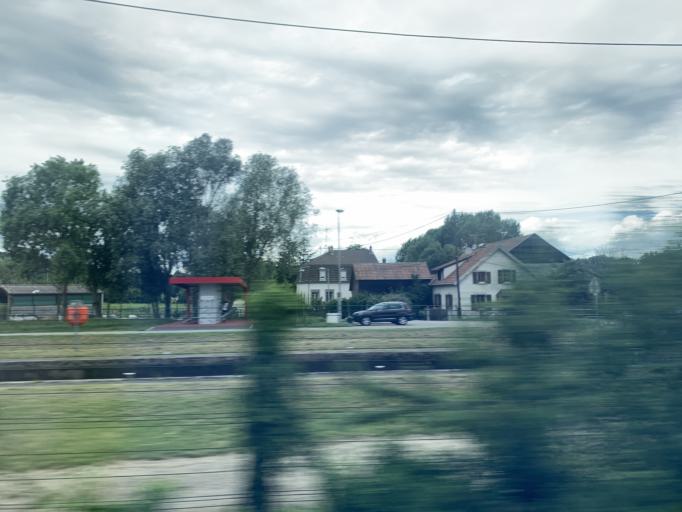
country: FR
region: Alsace
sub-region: Departement du Haut-Rhin
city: Brunstatt
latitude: 47.7187
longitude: 7.3139
